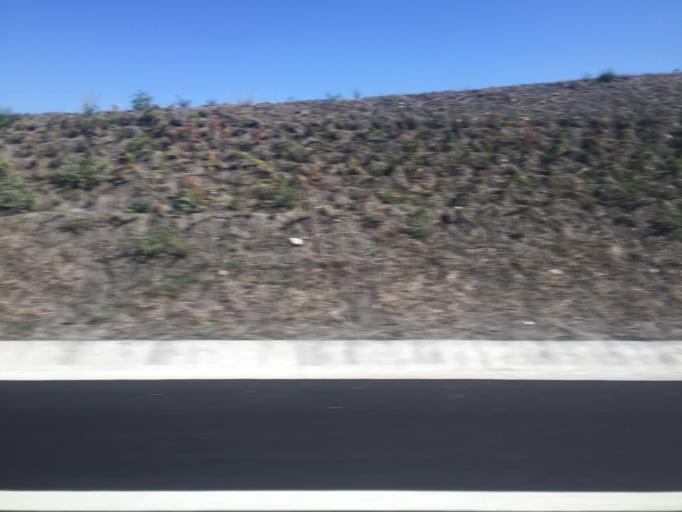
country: TR
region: Bursa
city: Mahmudiye
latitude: 40.2615
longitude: 28.6761
